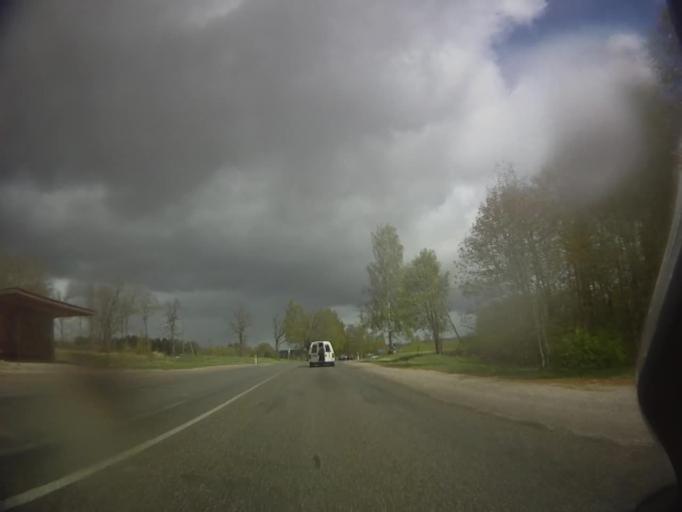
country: LV
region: Koceni
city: Koceni
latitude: 57.5163
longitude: 25.3475
